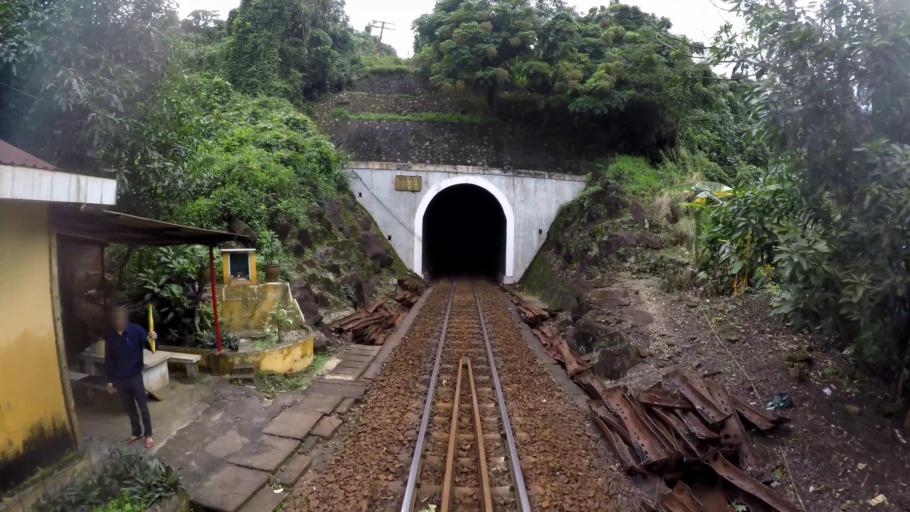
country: VN
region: Da Nang
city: Lien Chieu
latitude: 16.1722
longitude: 108.1438
